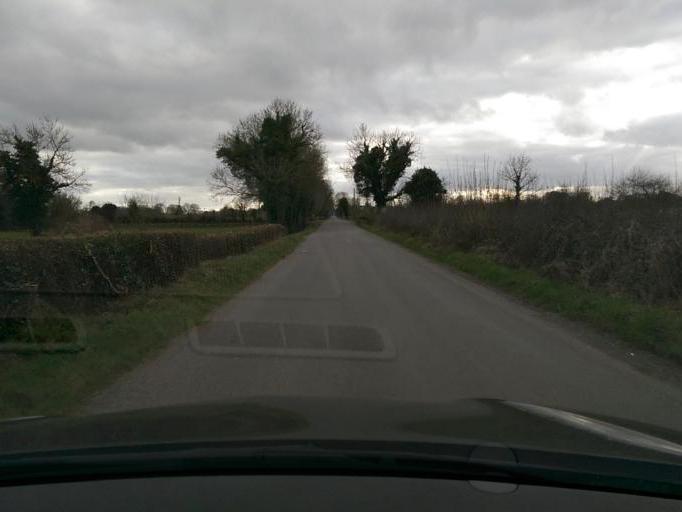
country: IE
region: Leinster
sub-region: Uibh Fhaili
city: Ferbane
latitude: 53.3658
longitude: -7.8435
